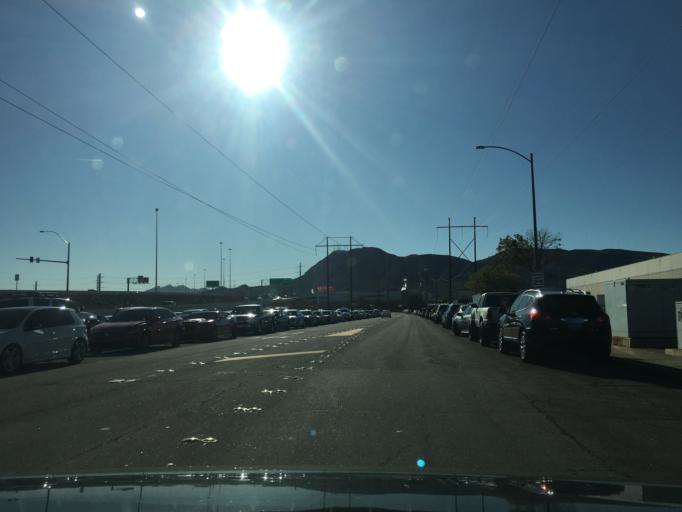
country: US
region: Nevada
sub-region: Clark County
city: Henderson
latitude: 36.0421
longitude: -115.0224
